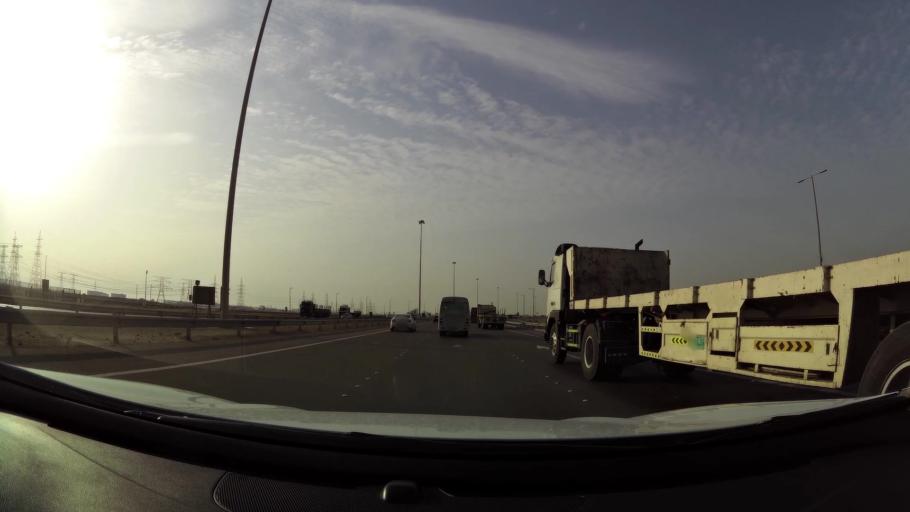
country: AE
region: Abu Dhabi
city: Abu Dhabi
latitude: 24.3053
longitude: 54.5322
